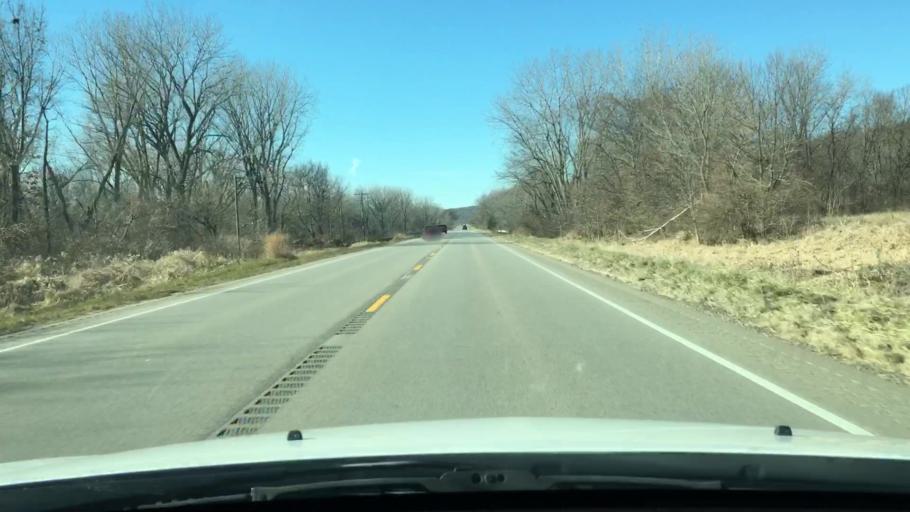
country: US
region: Illinois
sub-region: Peoria County
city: Glasford
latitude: 40.5508
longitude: -89.8214
